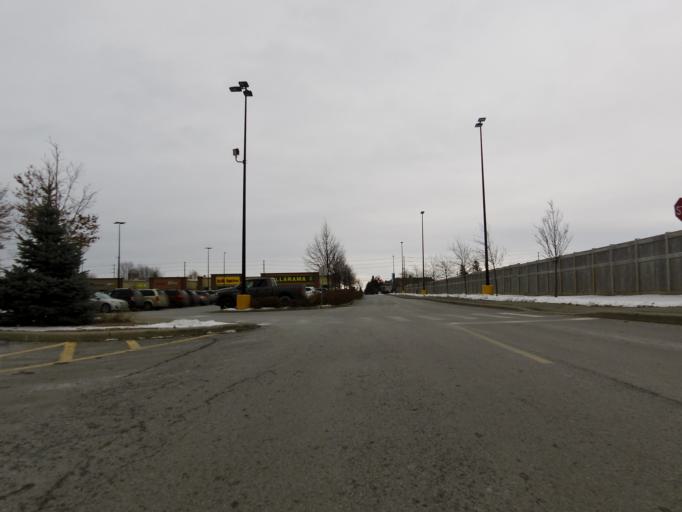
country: CA
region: Ontario
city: Bells Corners
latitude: 45.2743
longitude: -75.8730
